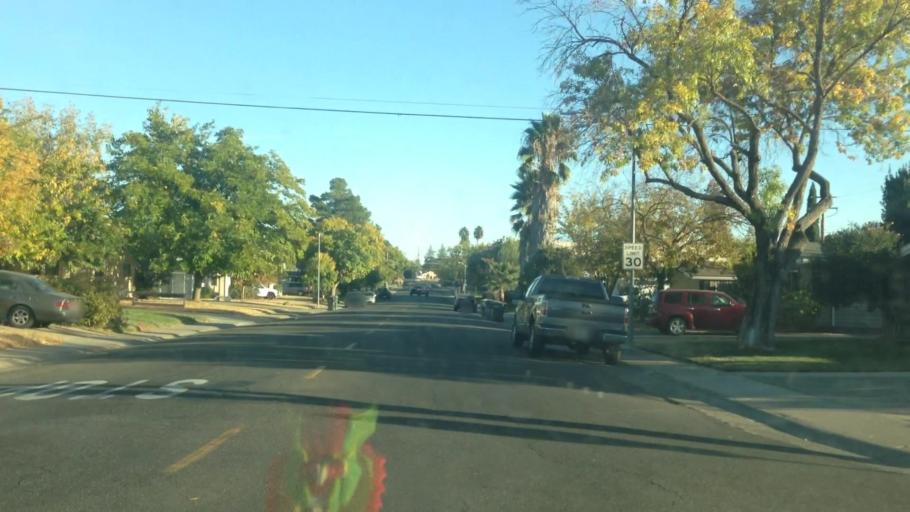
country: US
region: California
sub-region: Sacramento County
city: North Highlands
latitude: 38.6863
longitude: -121.3676
